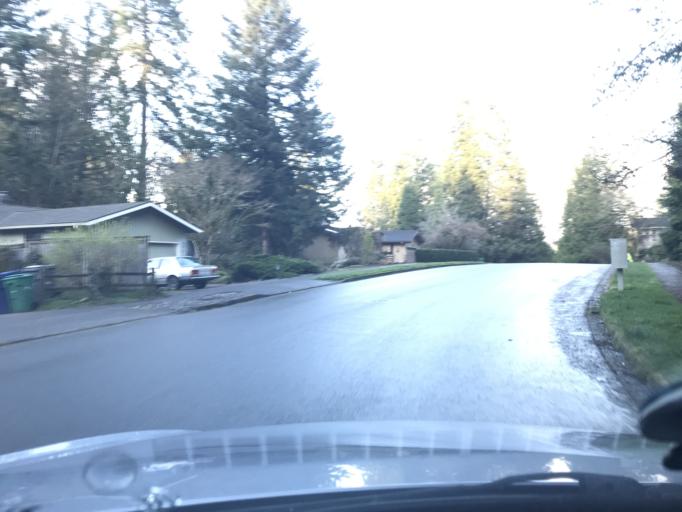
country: US
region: Washington
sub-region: King County
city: Sammamish
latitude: 47.6391
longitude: -122.1080
